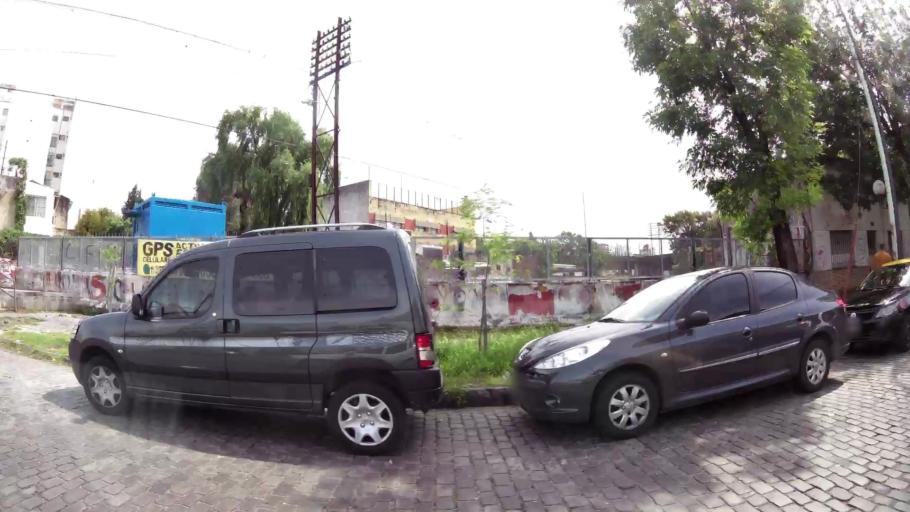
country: AR
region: Buenos Aires F.D.
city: Villa Santa Rita
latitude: -34.6354
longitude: -58.4957
